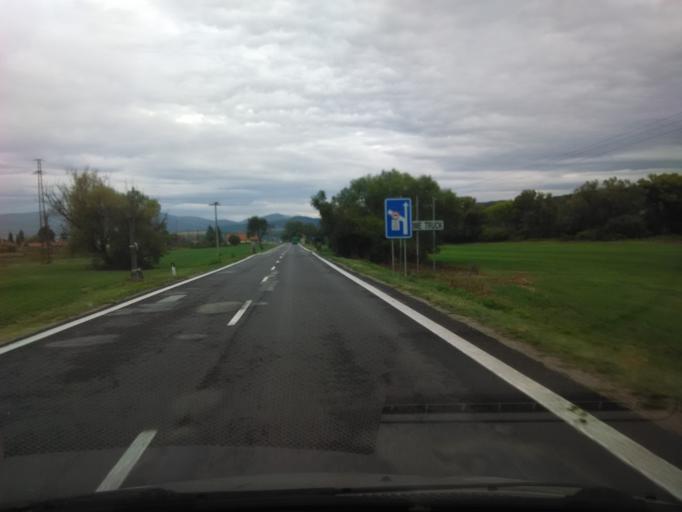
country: SK
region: Nitriansky
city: Tlmace
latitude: 48.3062
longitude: 18.5348
